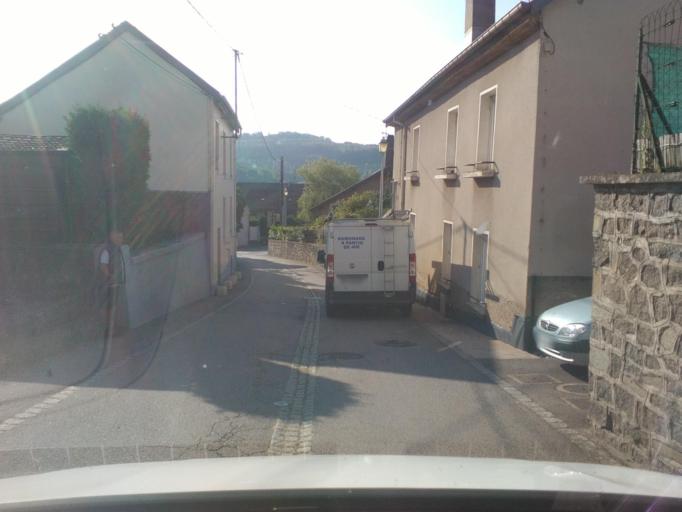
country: FR
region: Lorraine
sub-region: Departement des Vosges
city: Senones
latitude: 48.3976
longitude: 6.9755
